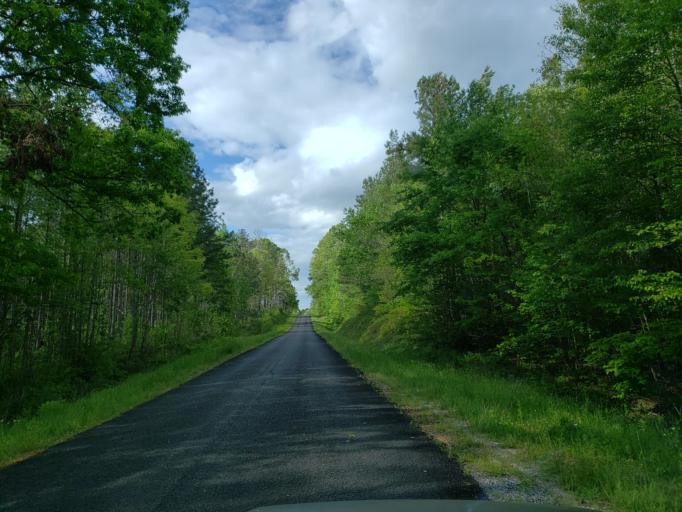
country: US
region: Georgia
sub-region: Haralson County
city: Tallapoosa
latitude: 33.7871
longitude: -85.3806
